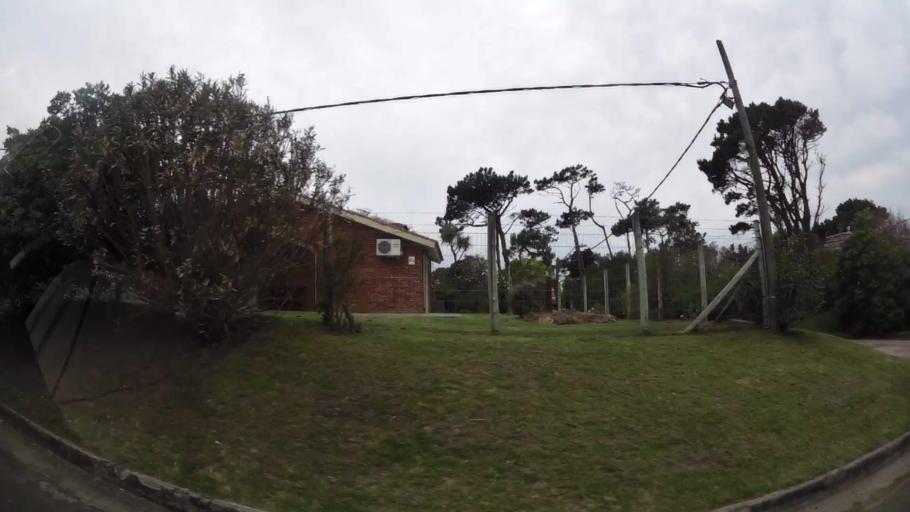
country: UY
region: Maldonado
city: Maldonado
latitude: -34.9169
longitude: -54.9730
